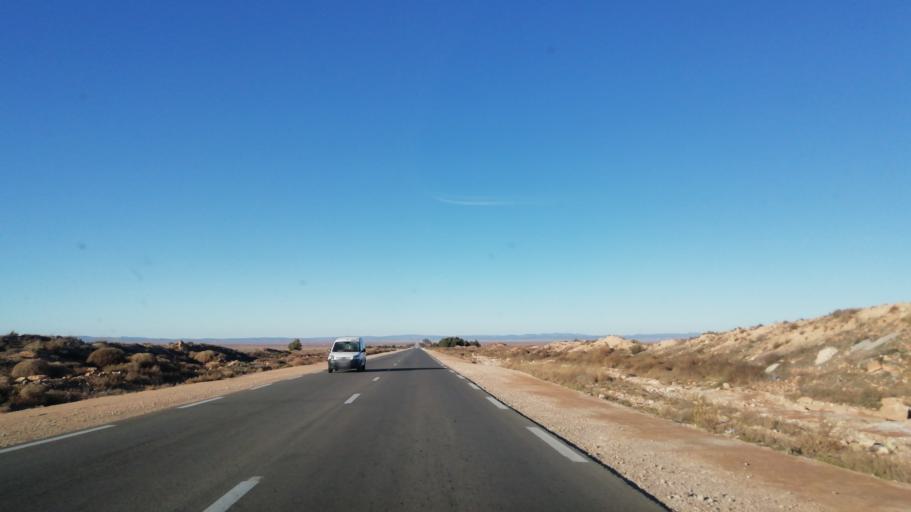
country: DZ
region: Tlemcen
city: Sebdou
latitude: 34.3100
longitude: -1.2621
